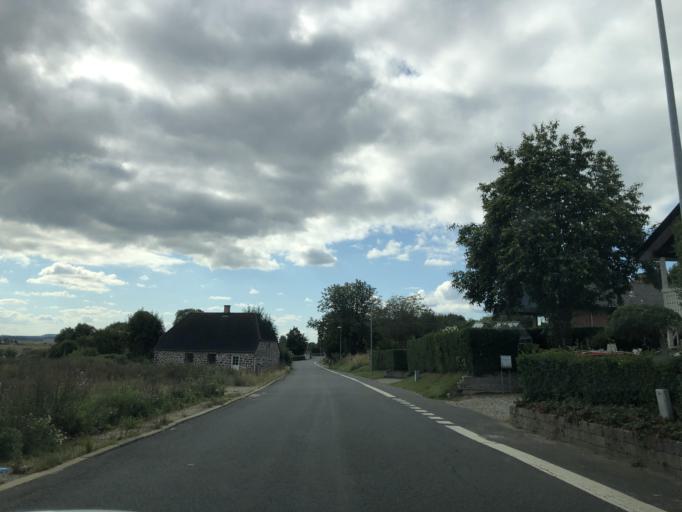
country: DK
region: Central Jutland
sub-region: Viborg Kommune
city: Viborg
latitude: 56.5807
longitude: 9.3853
